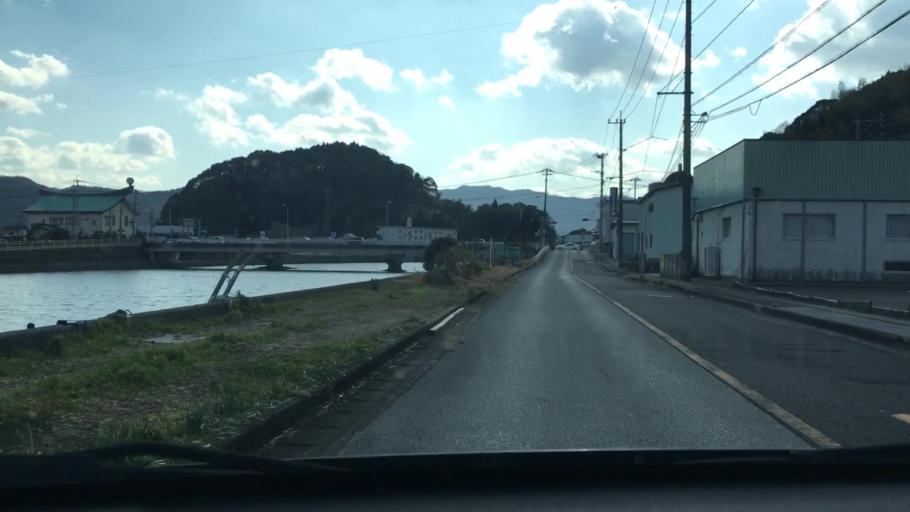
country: JP
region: Oita
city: Saiki
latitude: 32.9630
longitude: 131.9126
